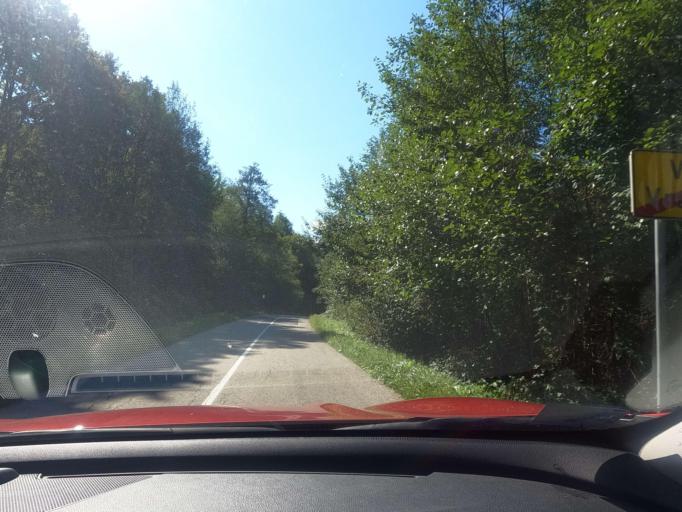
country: BA
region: Federation of Bosnia and Herzegovina
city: Vrnograc
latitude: 45.2729
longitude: 15.9728
